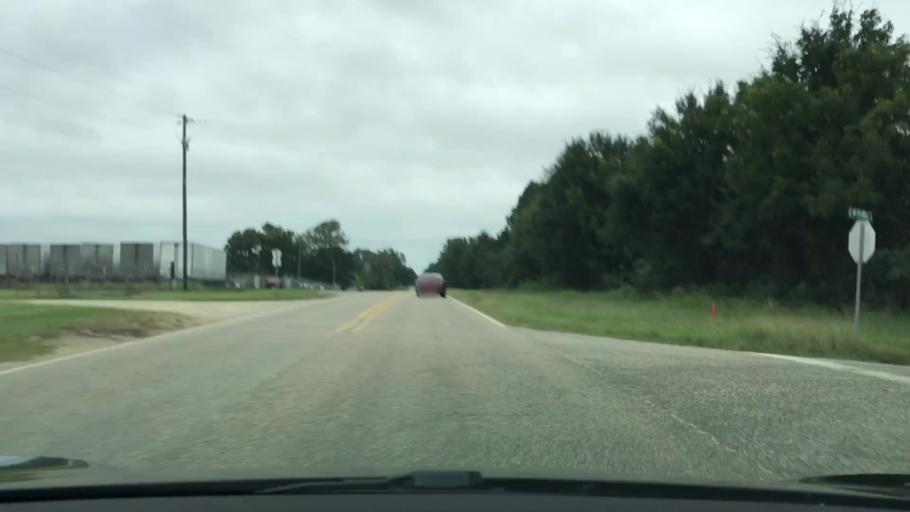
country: US
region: Alabama
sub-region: Geneva County
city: Samson
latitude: 31.1830
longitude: -86.1481
